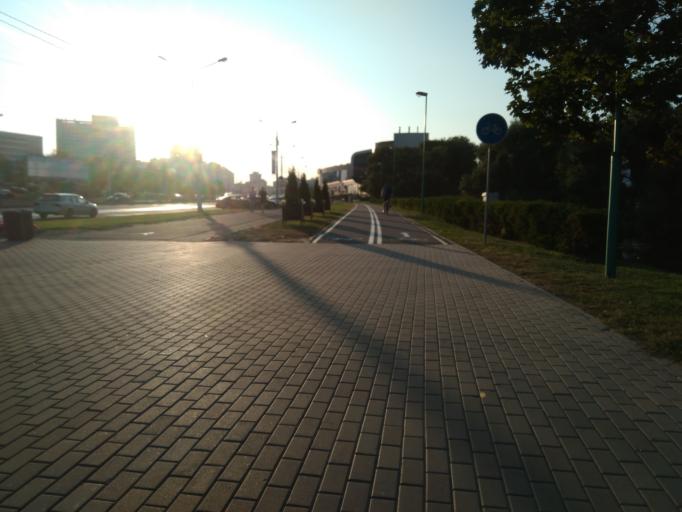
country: BY
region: Minsk
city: Zhdanovichy
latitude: 53.9370
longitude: 27.4940
